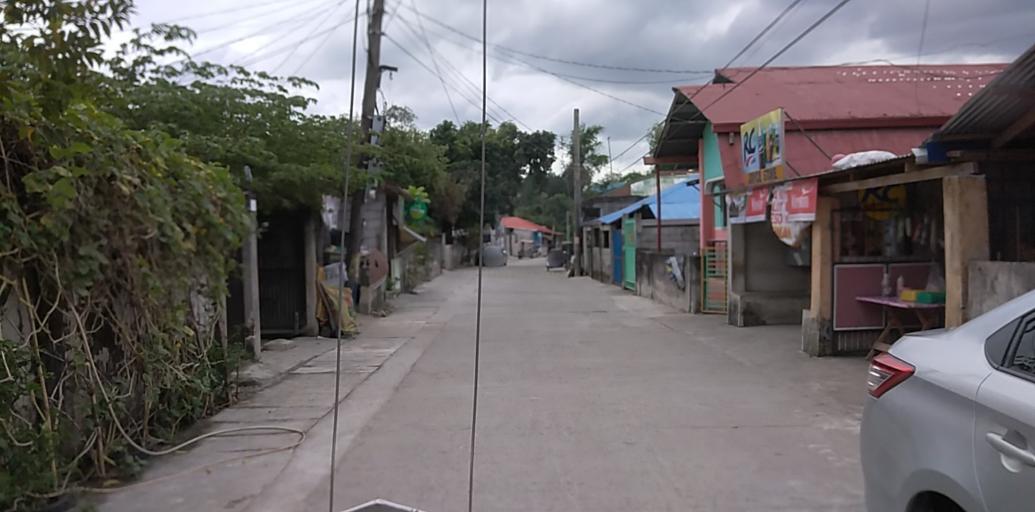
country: PH
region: Central Luzon
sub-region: Province of Pampanga
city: Porac
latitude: 15.0651
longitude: 120.5338
